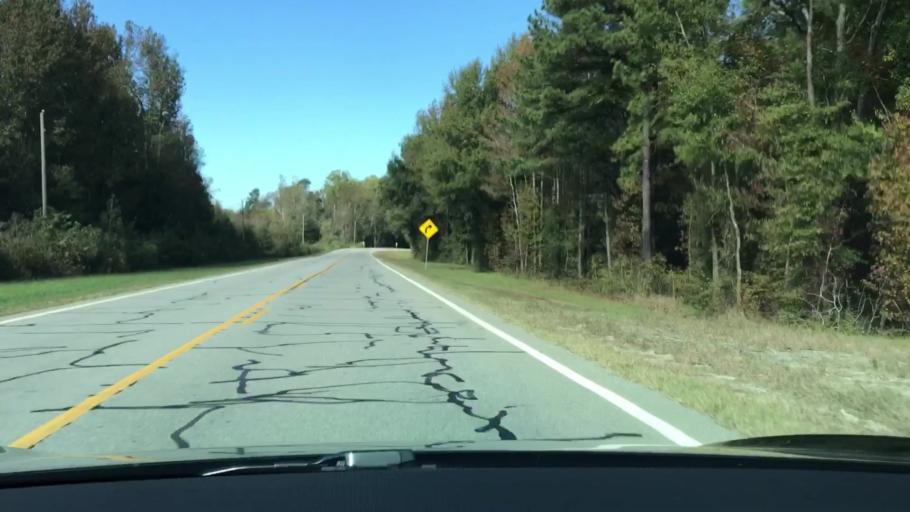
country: US
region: Georgia
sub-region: Glascock County
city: Gibson
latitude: 33.3325
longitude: -82.5645
